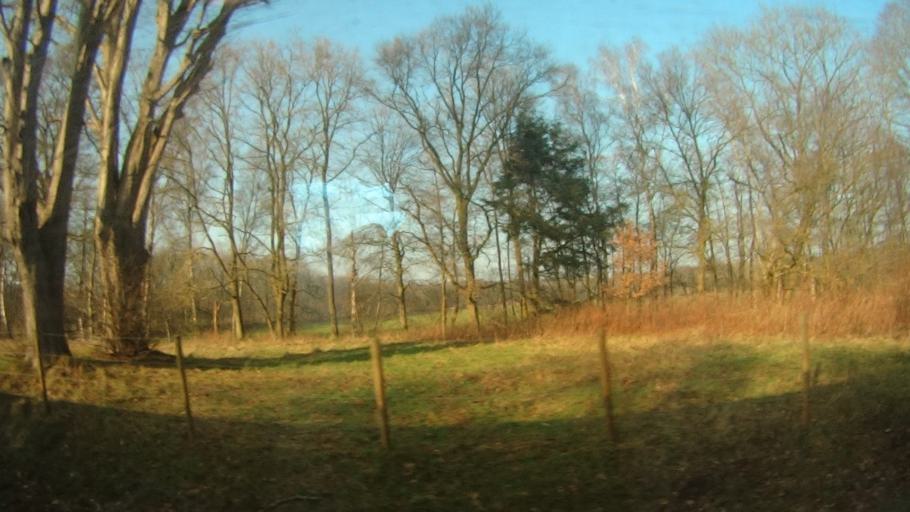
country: NL
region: Overijssel
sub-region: Gemeente Dalfsen
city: Dalfsen
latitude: 52.5045
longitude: 6.3574
